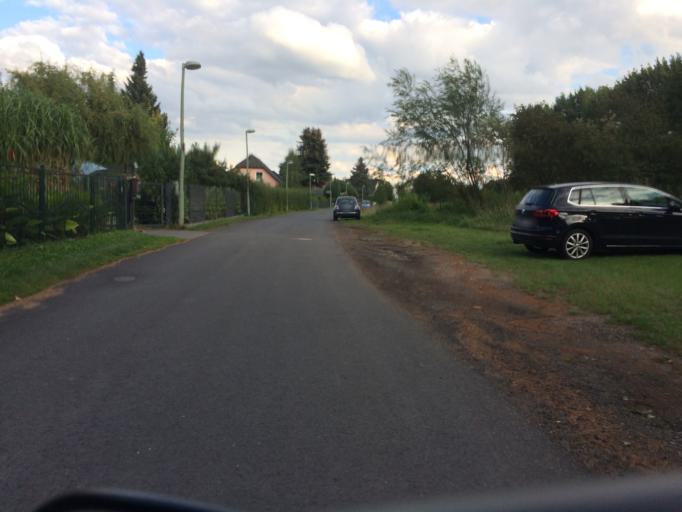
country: DE
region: Berlin
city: Blankenburg
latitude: 52.5886
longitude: 13.4618
